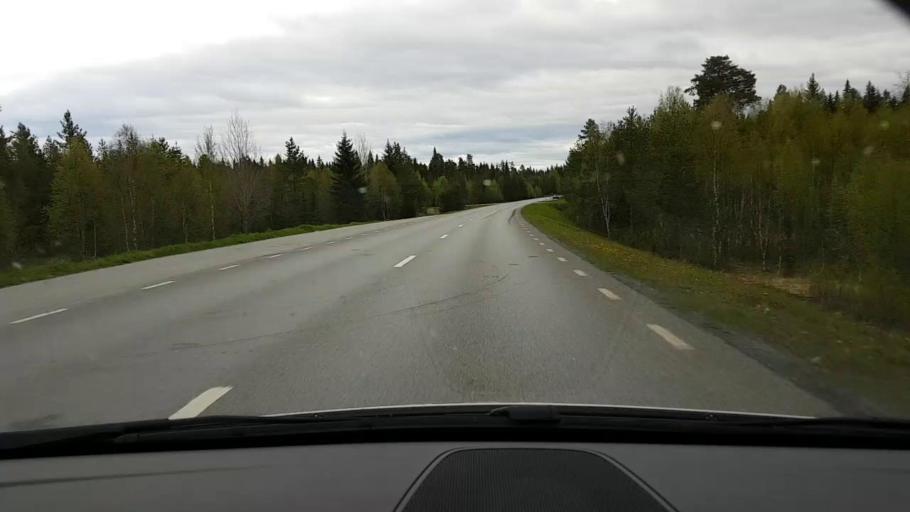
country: SE
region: Jaemtland
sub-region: Krokoms Kommun
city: Valla
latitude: 63.3060
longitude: 13.9228
